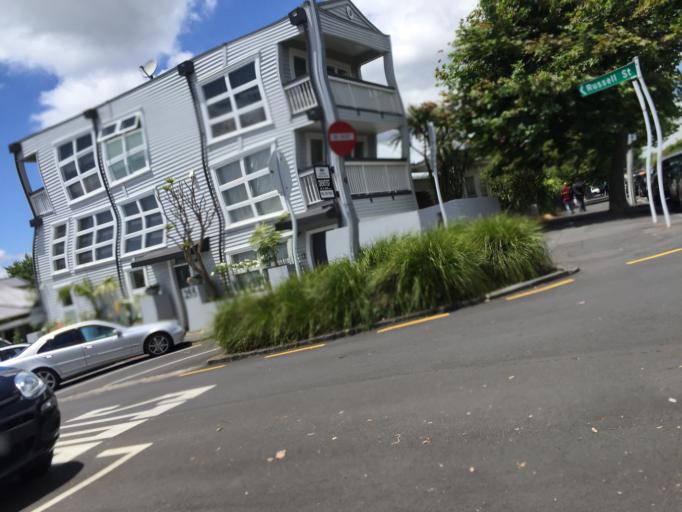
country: NZ
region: Auckland
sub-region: Auckland
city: Auckland
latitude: -36.8490
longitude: 174.7441
